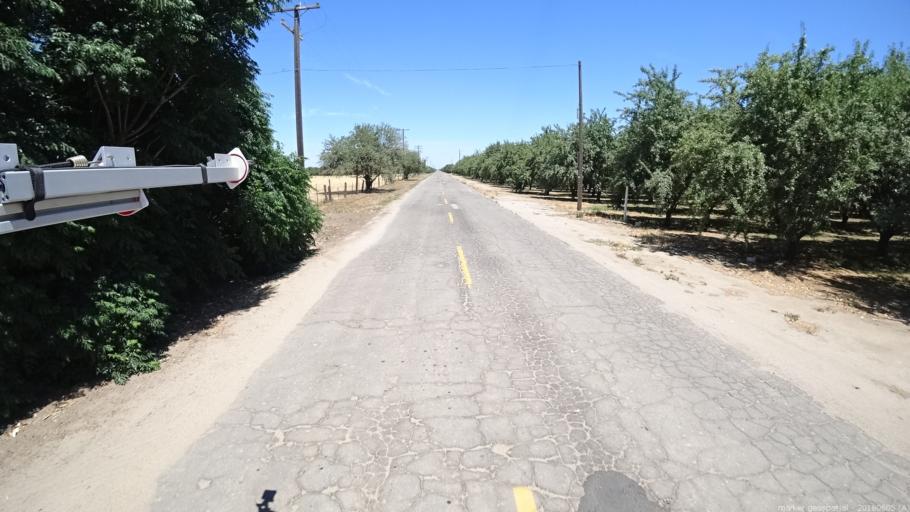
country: US
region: California
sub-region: Madera County
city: Chowchilla
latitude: 37.0907
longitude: -120.4210
